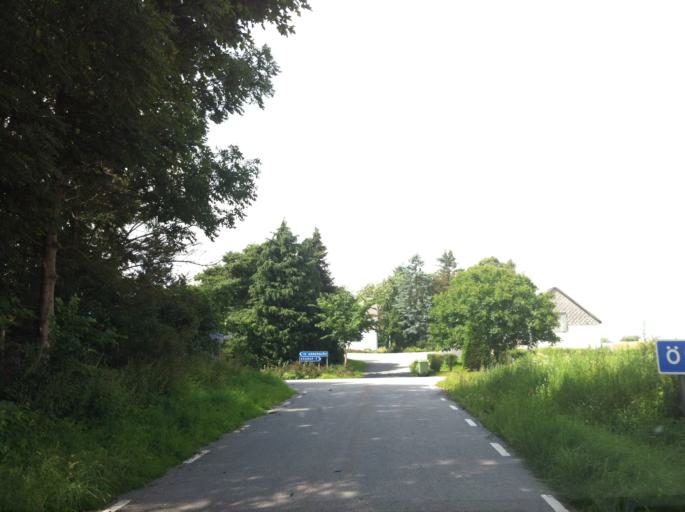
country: SE
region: Skane
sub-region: Skurups Kommun
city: Skurup
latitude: 55.4175
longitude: 13.4639
